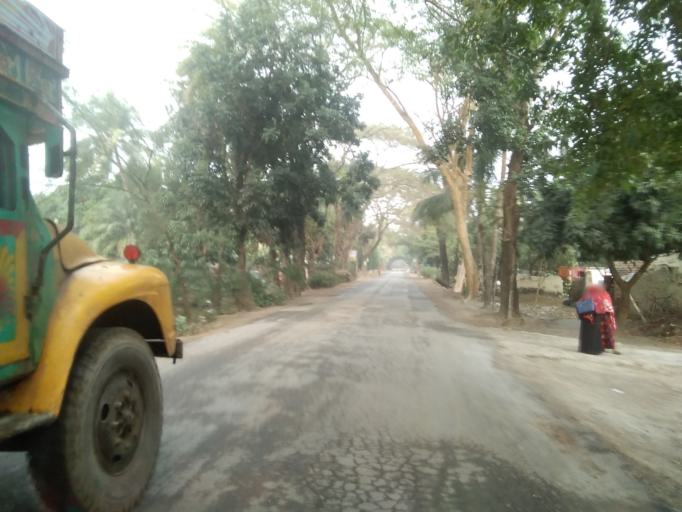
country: BD
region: Khulna
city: Satkhira
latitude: 22.6791
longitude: 89.0220
